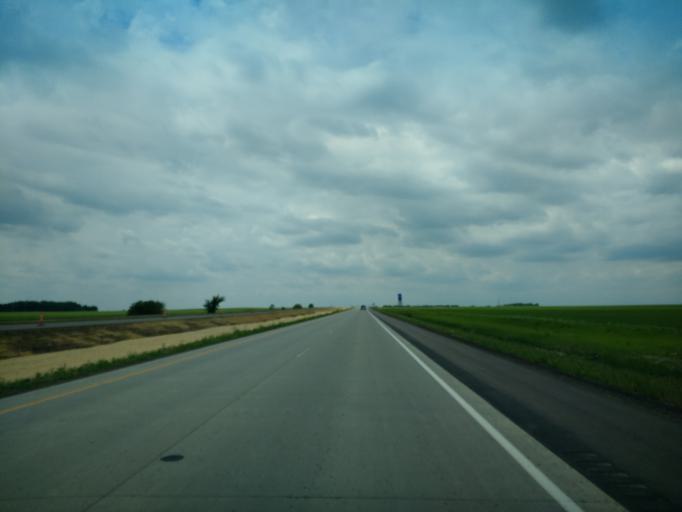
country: US
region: Minnesota
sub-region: Cottonwood County
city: Mountain Lake
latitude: 43.9213
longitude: -94.9905
